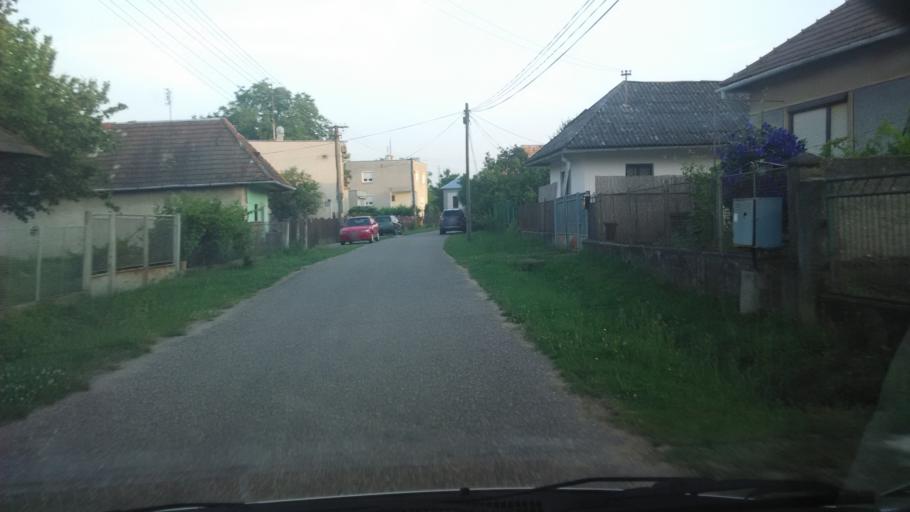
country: SK
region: Nitriansky
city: Tlmace
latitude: 48.1550
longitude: 18.4497
